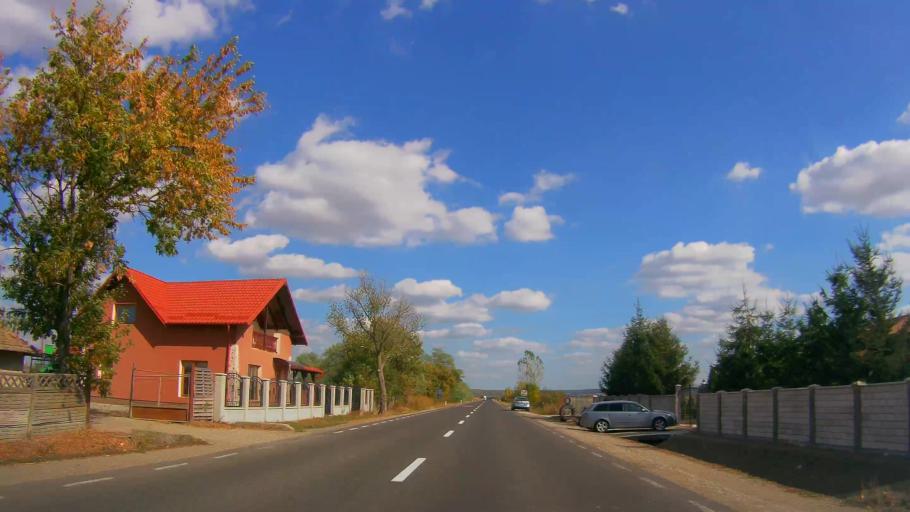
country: RO
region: Satu Mare
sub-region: Comuna Acas
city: Acas
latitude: 47.5407
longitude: 22.7925
